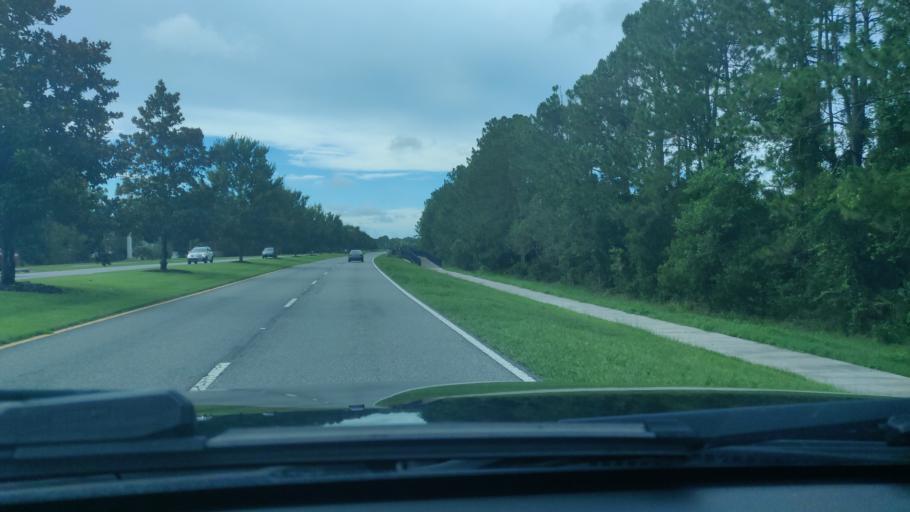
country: US
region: Florida
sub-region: Flagler County
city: Palm Coast
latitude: 29.5252
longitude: -81.2256
